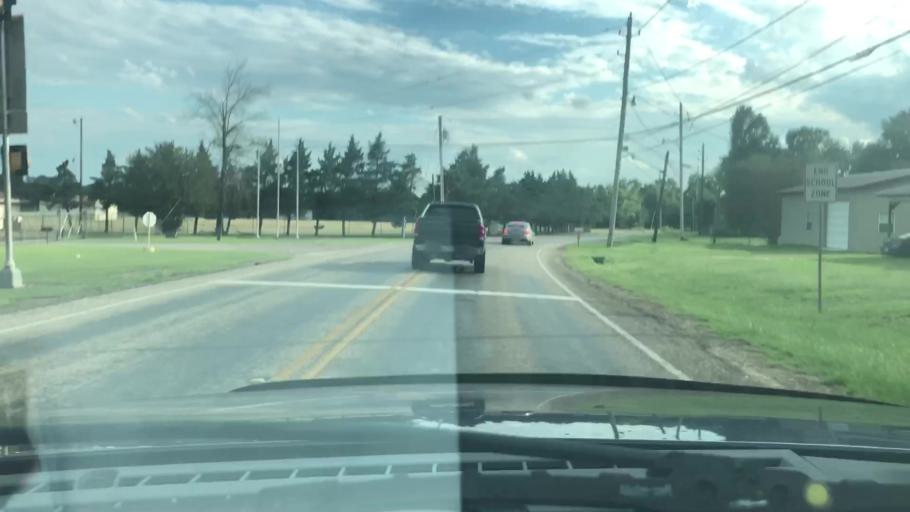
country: US
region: Texas
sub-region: Bowie County
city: Texarkana
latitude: 33.3936
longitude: -94.0649
